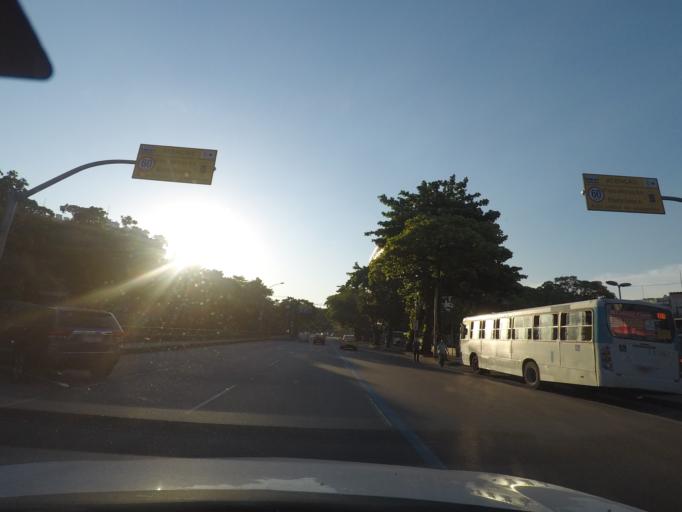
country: BR
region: Rio de Janeiro
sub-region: Rio De Janeiro
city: Rio de Janeiro
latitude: -22.9209
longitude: -43.2242
